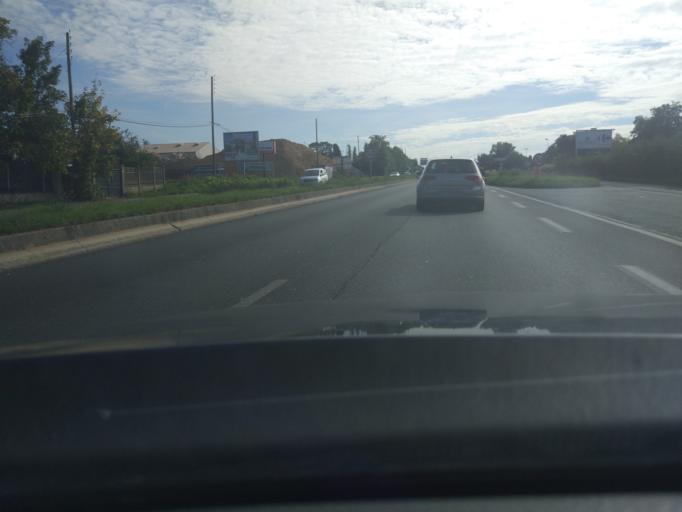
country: FR
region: Ile-de-France
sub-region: Departement de l'Essonne
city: La Ville-du-Bois
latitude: 48.6676
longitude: 2.2788
